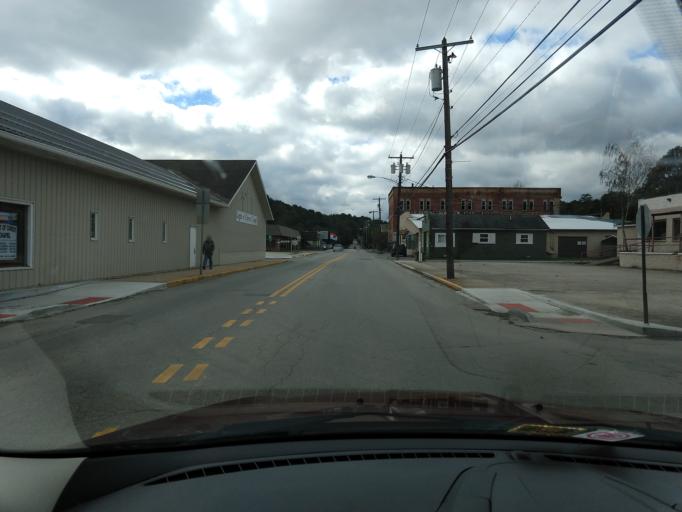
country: US
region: West Virginia
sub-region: Barbour County
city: Belington
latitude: 39.0244
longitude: -79.9360
